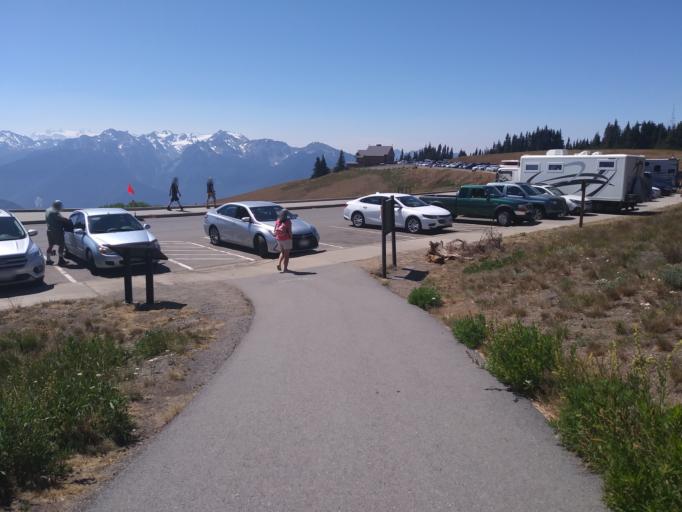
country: US
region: Washington
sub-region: Clallam County
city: Port Angeles
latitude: 47.9701
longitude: -123.4950
